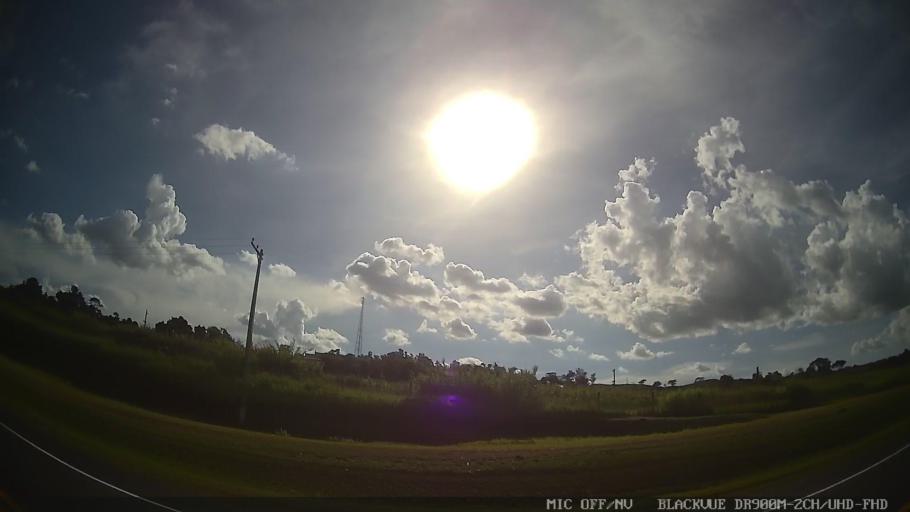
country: BR
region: Sao Paulo
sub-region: Laranjal Paulista
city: Laranjal Paulista
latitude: -23.0614
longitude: -47.8226
